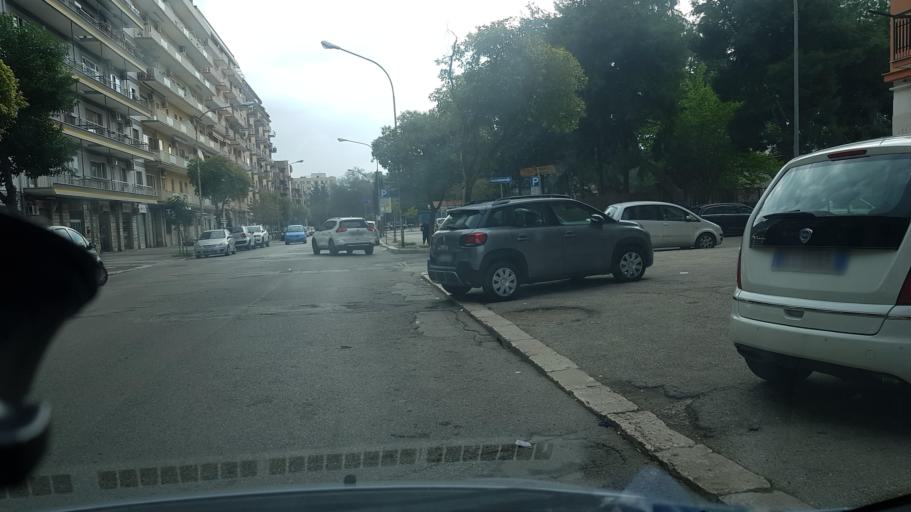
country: IT
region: Apulia
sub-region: Provincia di Foggia
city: Foggia
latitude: 41.4548
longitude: 15.5595
